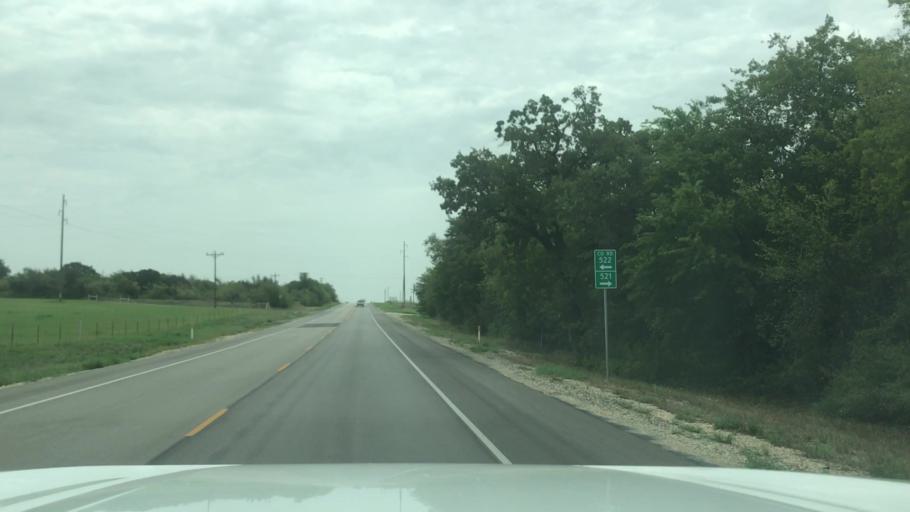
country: US
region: Texas
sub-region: Erath County
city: Dublin
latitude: 32.0885
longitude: -98.2595
